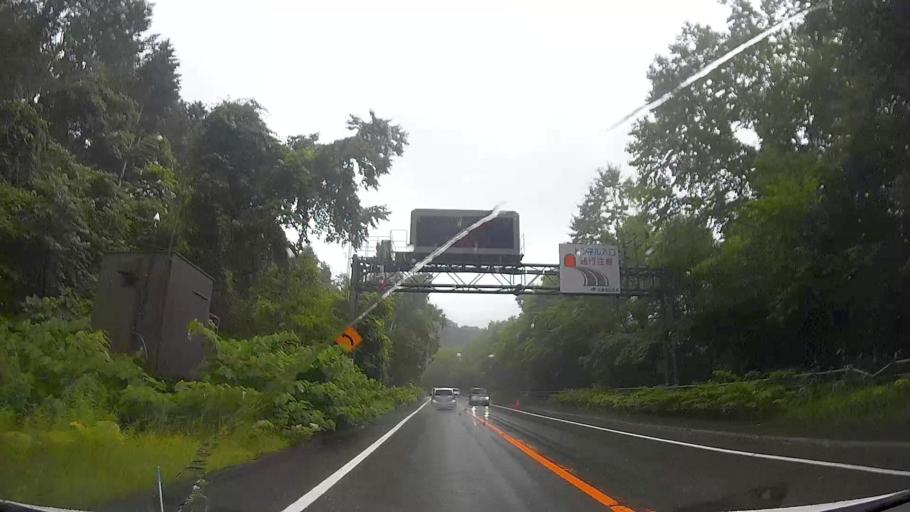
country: JP
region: Hokkaido
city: Shiraoi
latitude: 42.7213
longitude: 141.2591
